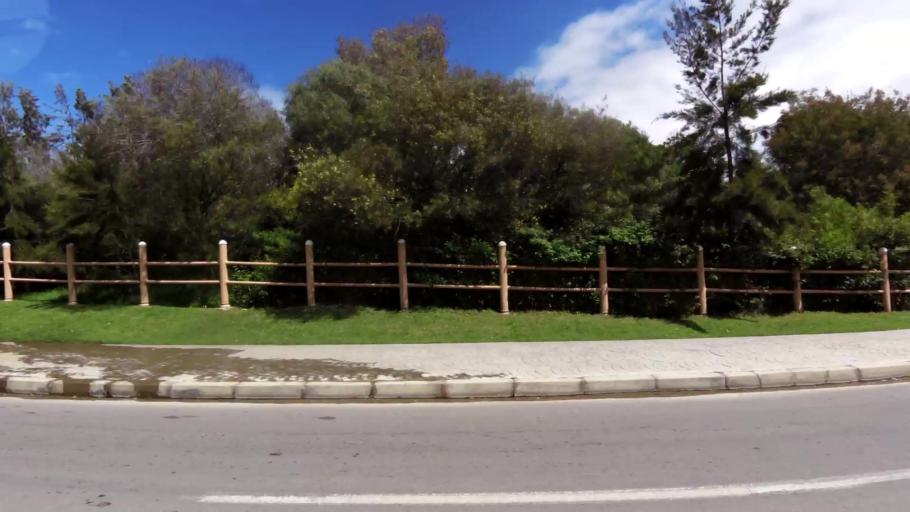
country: MA
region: Tanger-Tetouan
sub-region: Tanger-Assilah
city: Boukhalef
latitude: 35.7844
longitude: -5.8654
